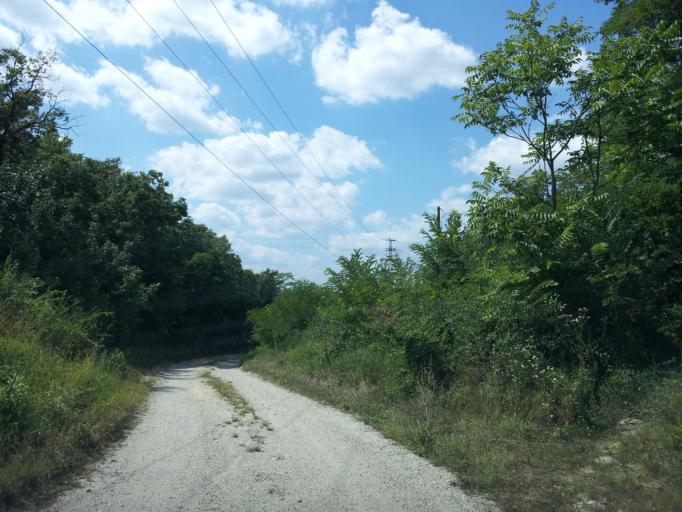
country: HU
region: Veszprem
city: Balatonkenese
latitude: 47.0424
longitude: 18.0903
